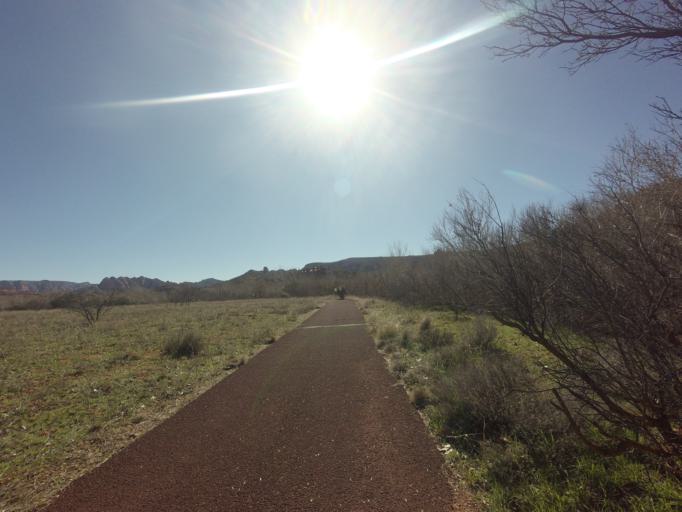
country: US
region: Arizona
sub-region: Yavapai County
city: West Sedona
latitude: 34.8102
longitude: -111.8282
